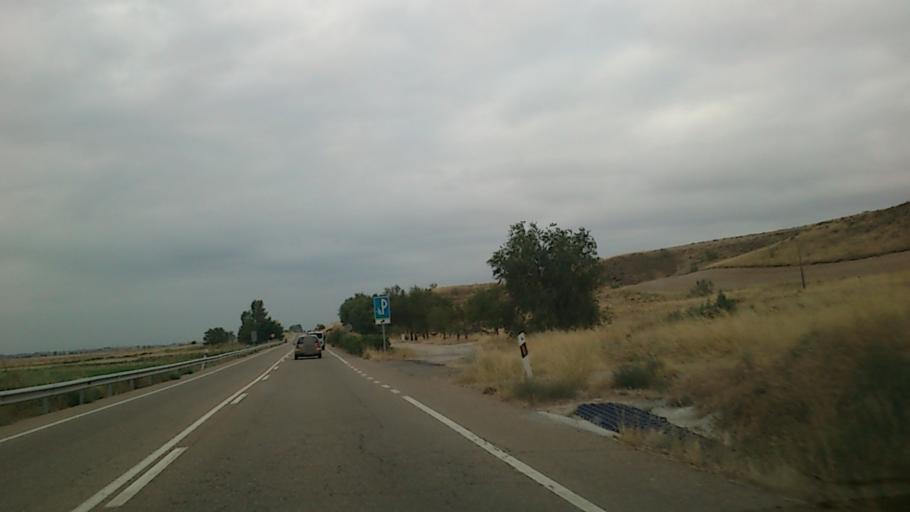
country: ES
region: Aragon
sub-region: Provincia de Zaragoza
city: San Mateo de Gallego
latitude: 41.8129
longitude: -0.8056
